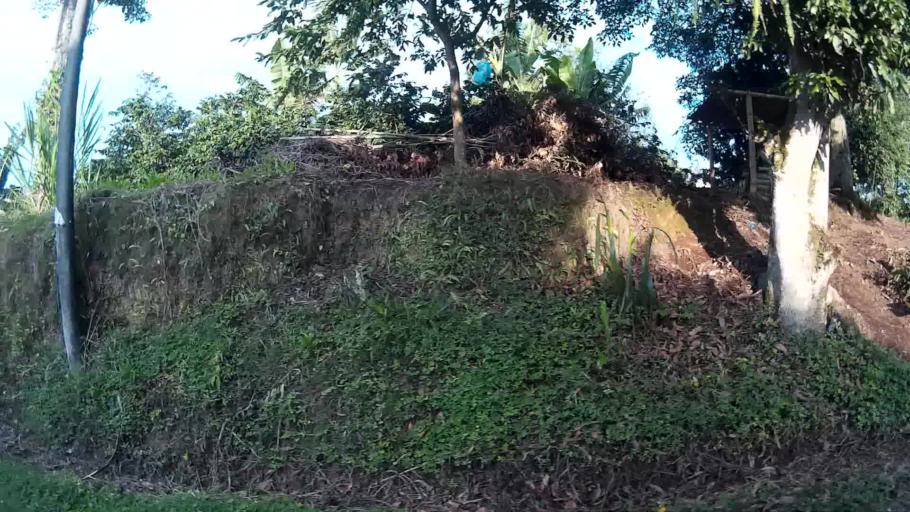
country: CO
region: Valle del Cauca
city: Ulloa
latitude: 4.7572
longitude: -75.7445
